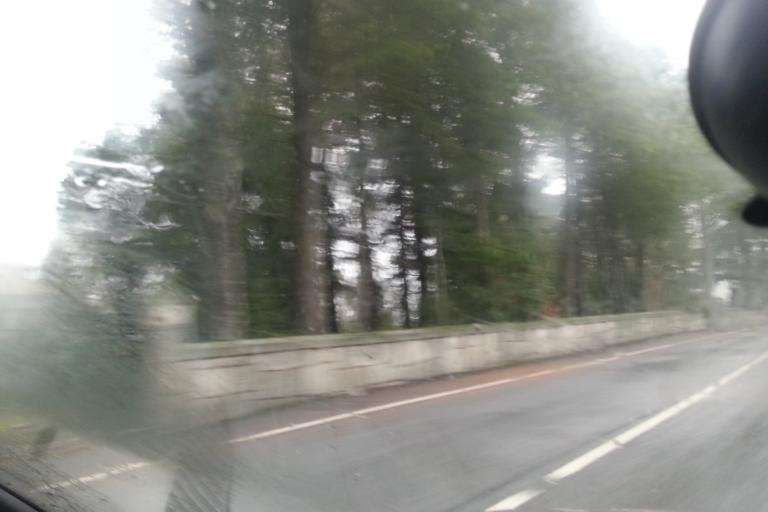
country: PT
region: Guarda
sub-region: Manteigas
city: Manteigas
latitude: 40.5002
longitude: -7.5885
